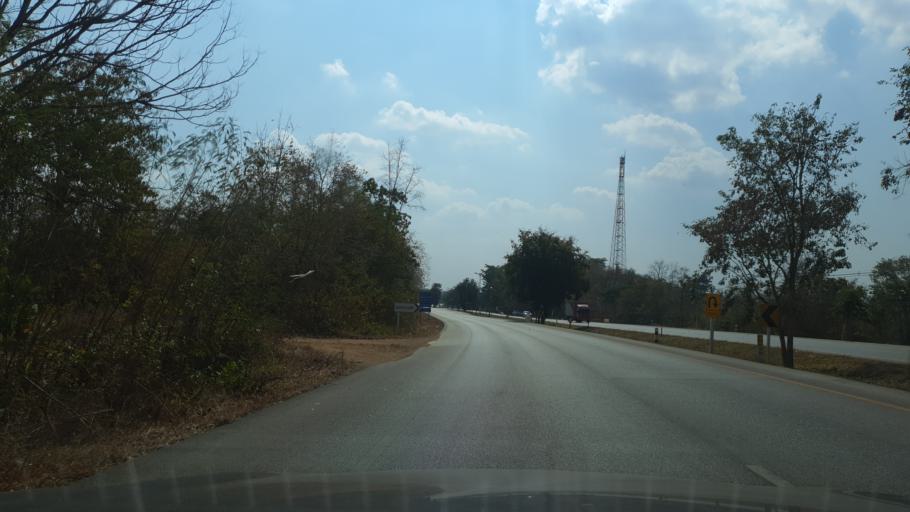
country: TH
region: Lampang
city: Mae Phrik
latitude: 17.4065
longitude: 99.1494
